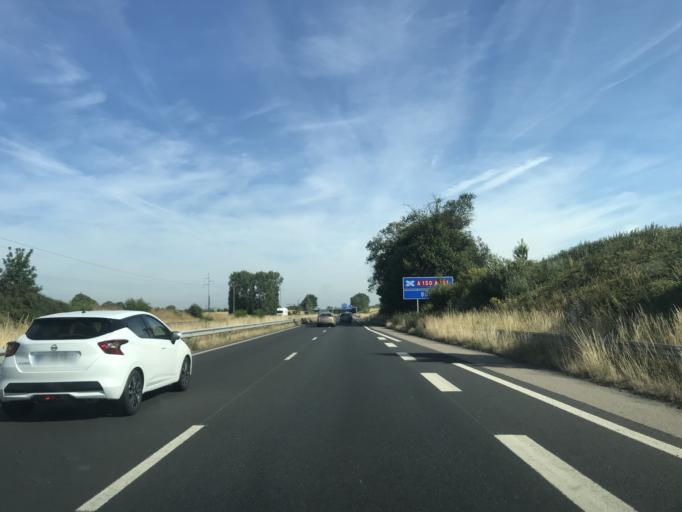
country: FR
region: Haute-Normandie
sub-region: Departement de la Seine-Maritime
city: La Vaupaliere
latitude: 49.4992
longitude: 0.9948
